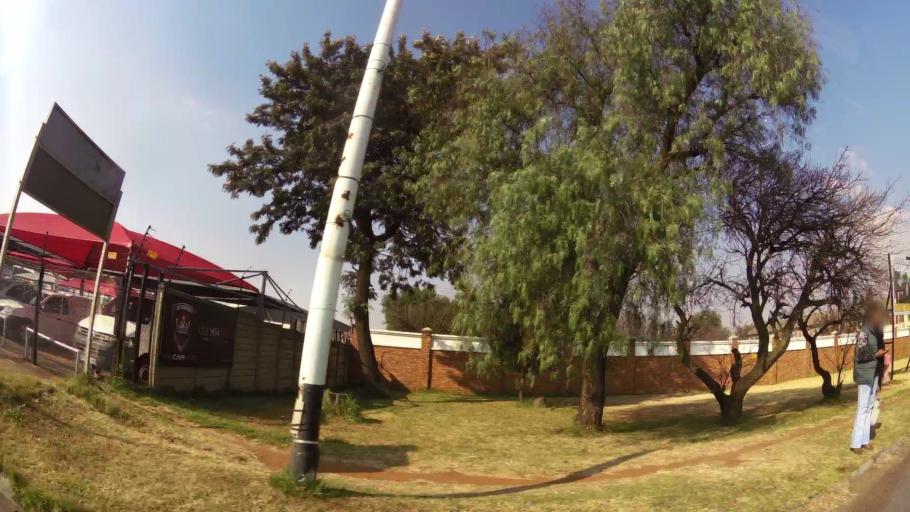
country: ZA
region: Gauteng
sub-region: Ekurhuleni Metropolitan Municipality
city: Boksburg
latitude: -26.1939
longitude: 28.2539
